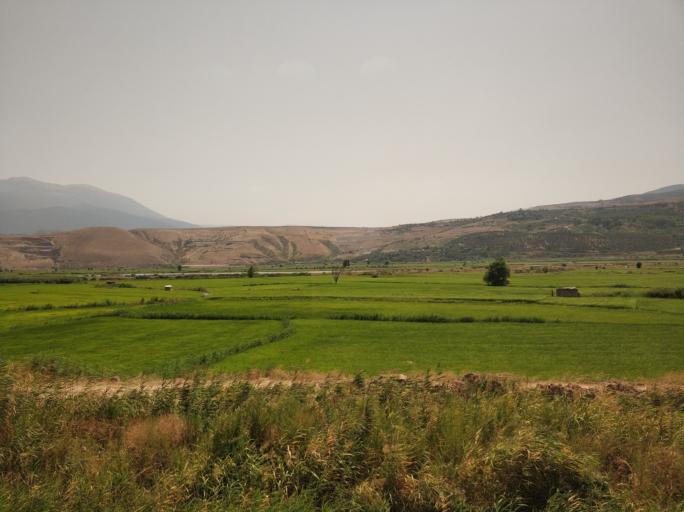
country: IR
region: Gilan
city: Pa'in-e Bazar-e Rudbar
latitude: 36.8821
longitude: 49.4982
